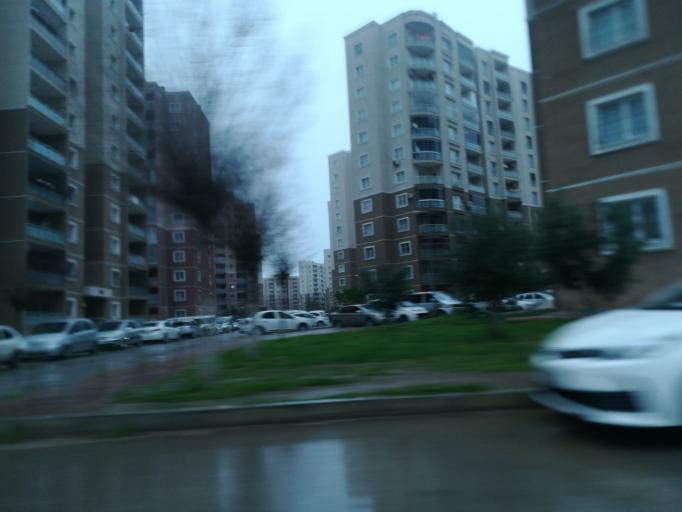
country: TR
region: Adana
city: Seyhan
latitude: 37.0073
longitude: 35.2796
